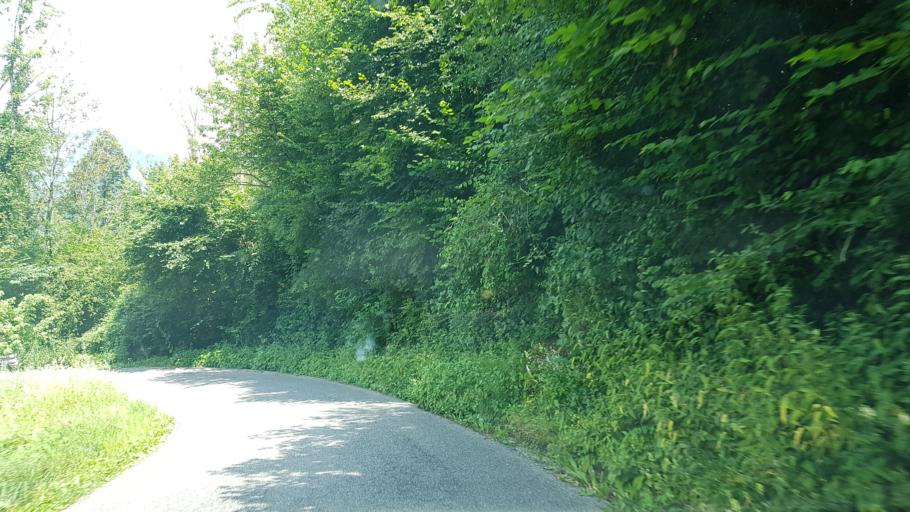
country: IT
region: Friuli Venezia Giulia
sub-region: Provincia di Udine
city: Lusevera
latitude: 46.2530
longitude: 13.2592
